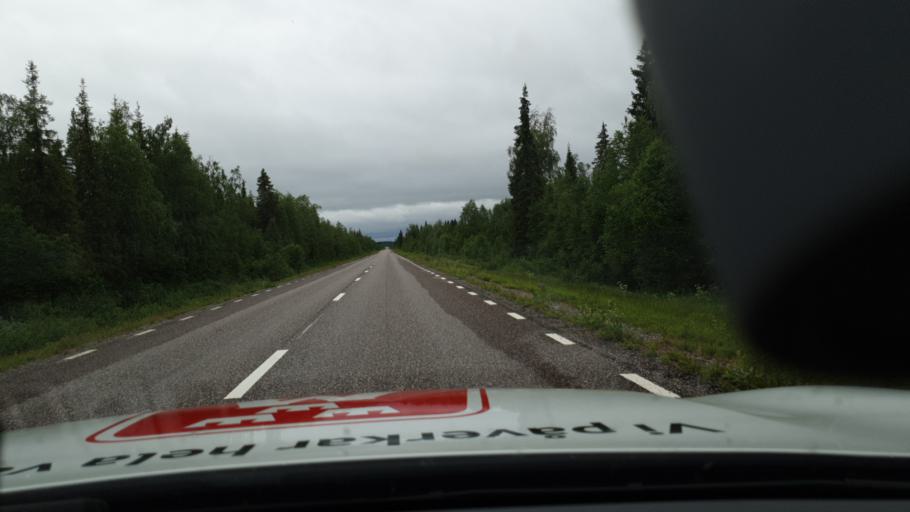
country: SE
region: Norrbotten
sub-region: Pajala Kommun
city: Pajala
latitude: 67.1290
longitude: 23.5912
